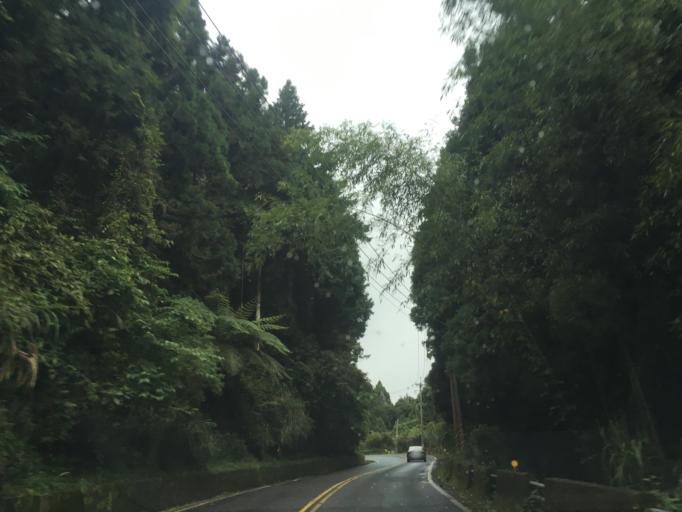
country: TW
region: Taiwan
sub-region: Chiayi
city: Jiayi Shi
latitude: 23.4922
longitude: 120.6996
